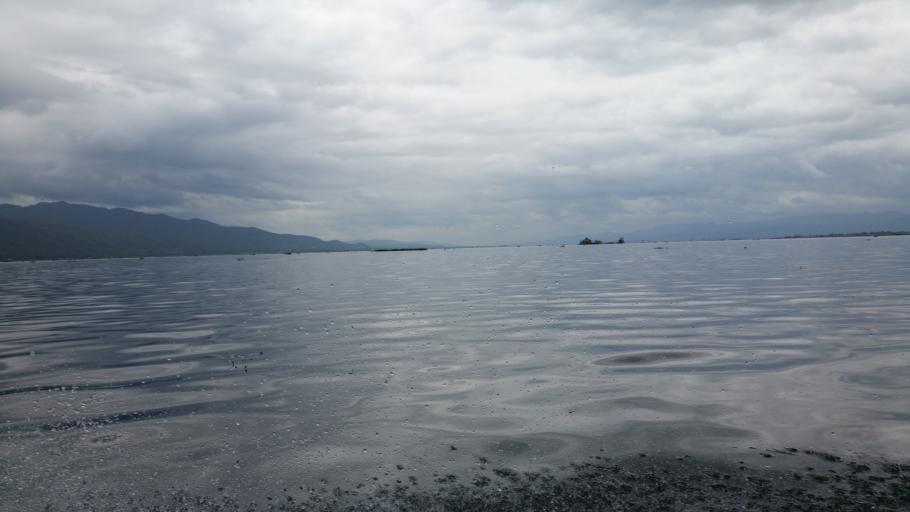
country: MM
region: Shan
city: Taunggyi
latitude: 20.5860
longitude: 96.9186
